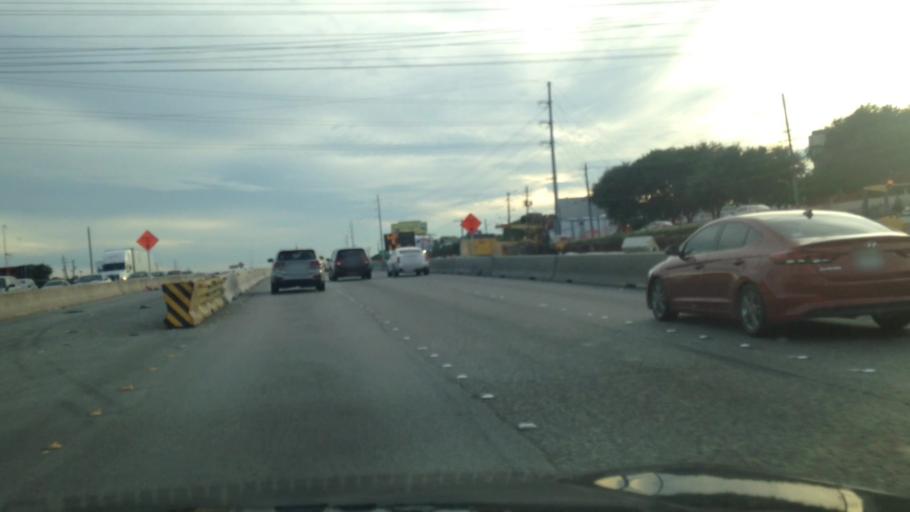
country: US
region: Texas
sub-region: Travis County
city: Onion Creek
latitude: 30.1885
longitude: -97.7720
